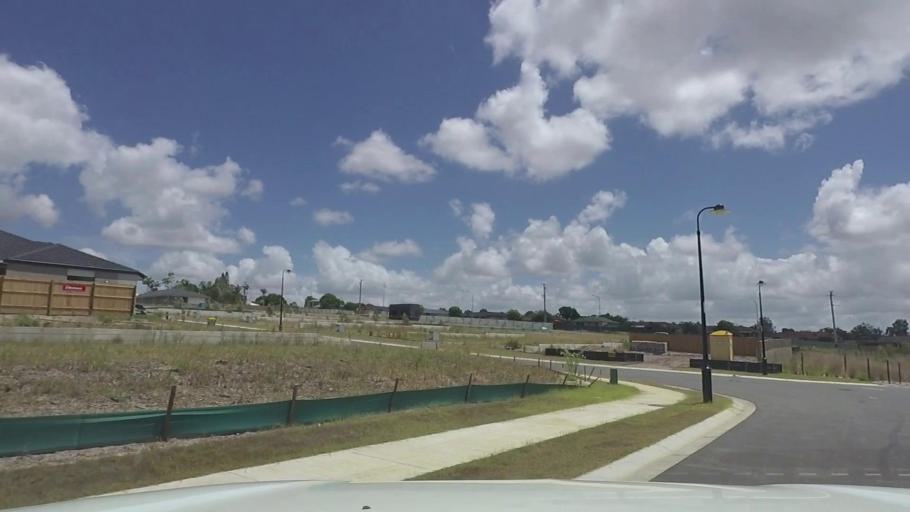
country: AU
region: Queensland
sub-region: Logan
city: Park Ridge South
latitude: -27.6913
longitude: 153.0559
